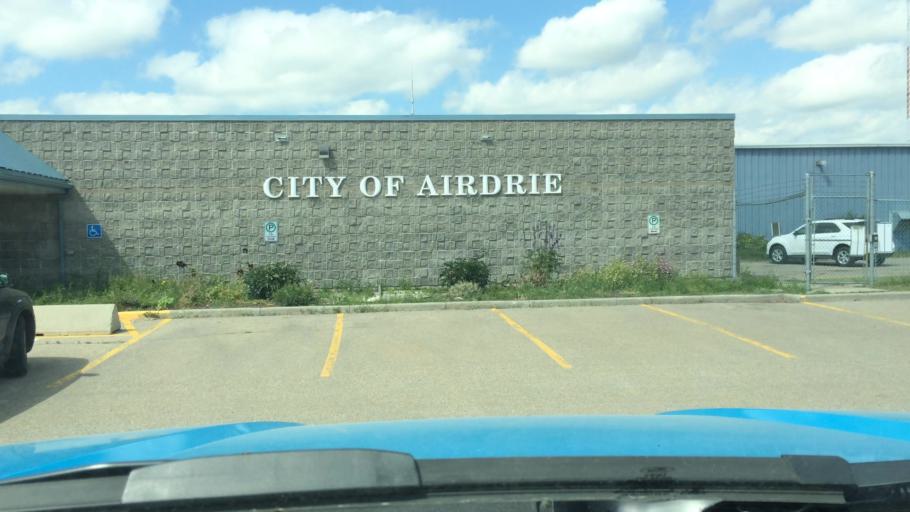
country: CA
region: Alberta
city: Airdrie
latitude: 51.2874
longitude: -113.9830
